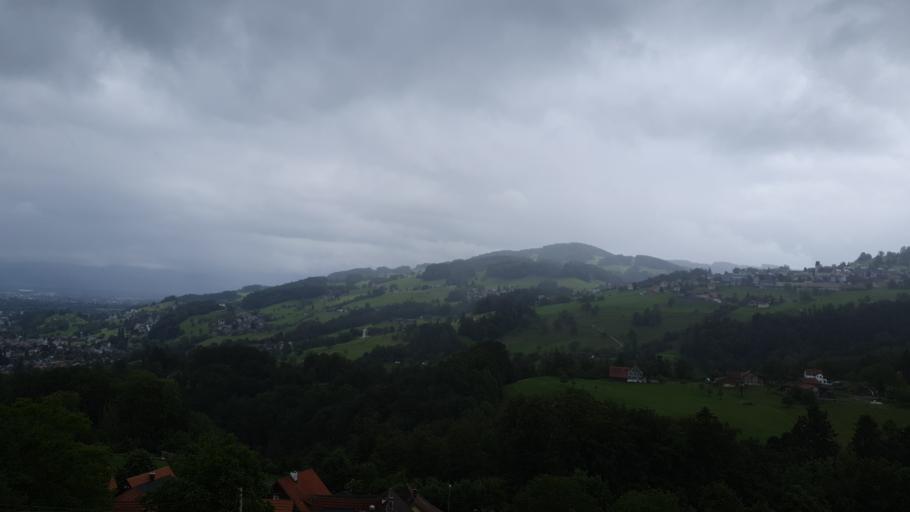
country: CH
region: Appenzell Ausserrhoden
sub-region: Bezirk Vorderland
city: Heiden
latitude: 47.4652
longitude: 9.5402
